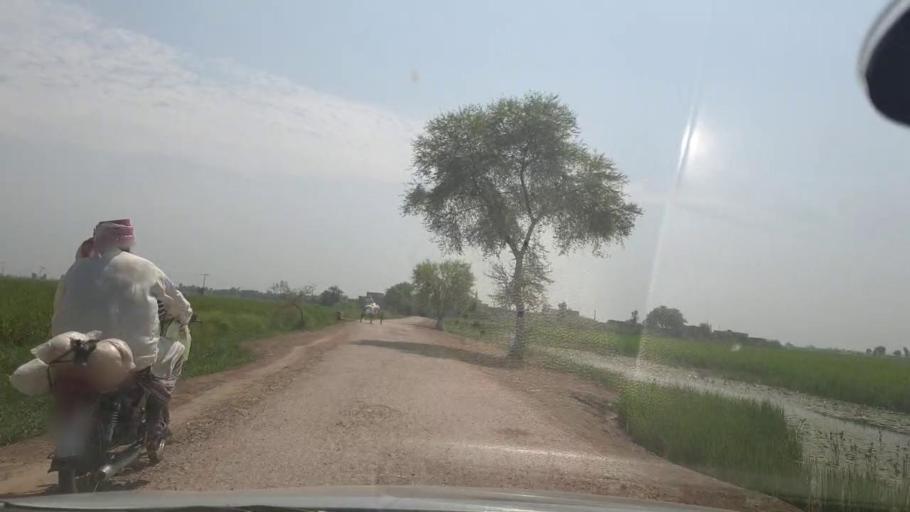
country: PK
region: Sindh
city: Thul
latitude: 28.1639
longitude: 68.6514
